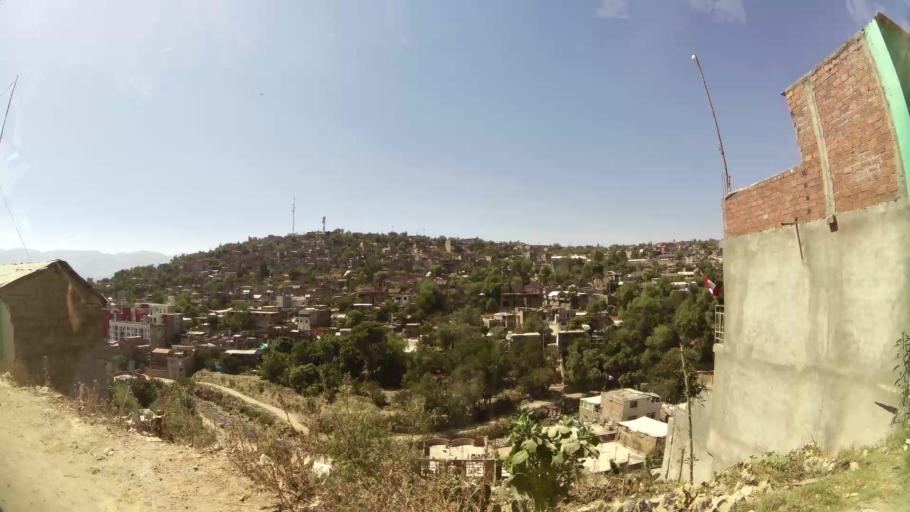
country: PE
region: Ayacucho
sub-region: Provincia de Huamanga
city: Carmen Alto
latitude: -13.1738
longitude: -74.2285
